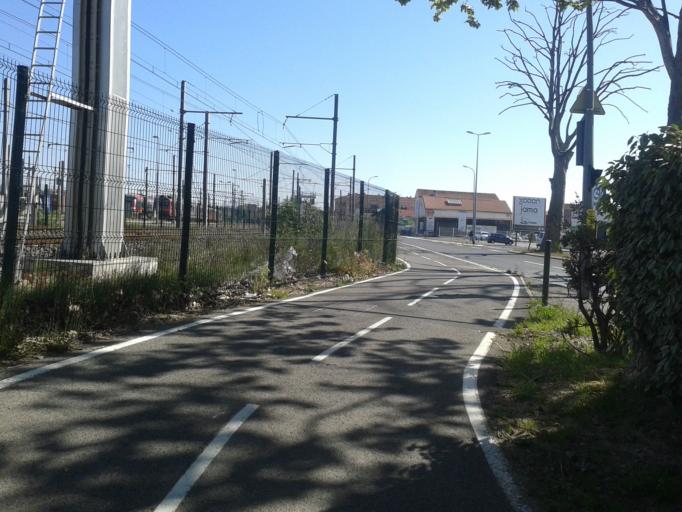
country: FR
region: Languedoc-Roussillon
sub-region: Departement des Pyrenees-Orientales
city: Perpignan
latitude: 42.6884
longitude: 2.8749
